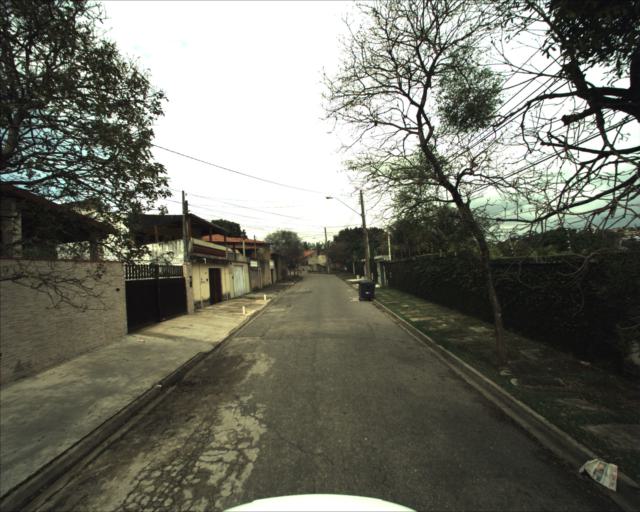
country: BR
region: Sao Paulo
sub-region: Sorocaba
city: Sorocaba
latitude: -23.5015
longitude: -47.4979
